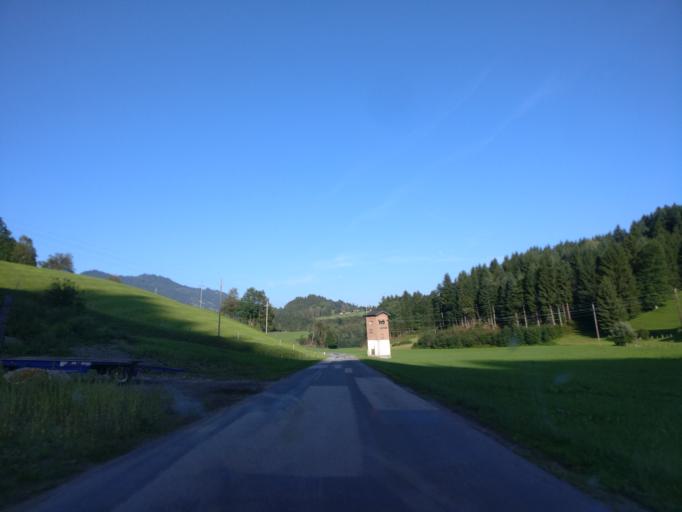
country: AT
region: Salzburg
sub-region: Politischer Bezirk Zell am See
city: Lend
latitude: 47.3231
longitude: 13.0682
